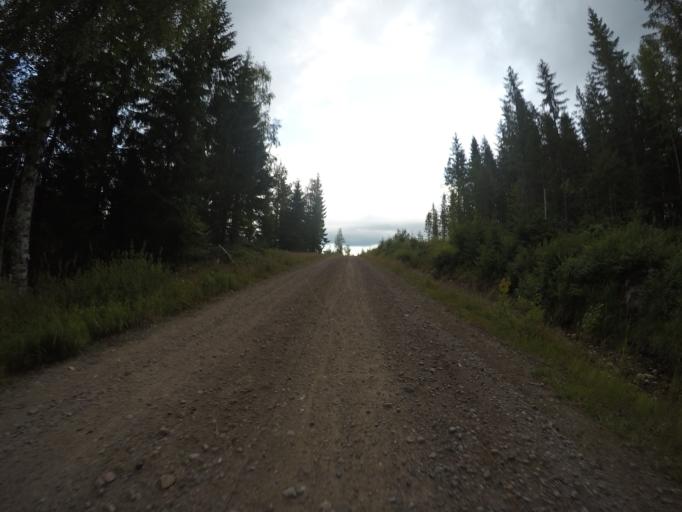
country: SE
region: Vaermland
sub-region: Filipstads Kommun
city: Lesjofors
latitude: 60.1980
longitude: 14.3883
